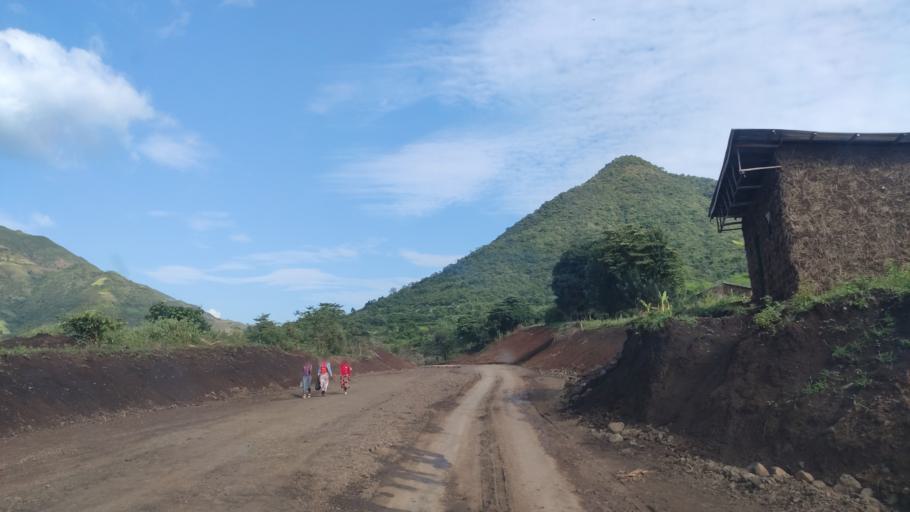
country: ET
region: Southern Nations, Nationalities, and People's Region
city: Arba Minch'
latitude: 6.4255
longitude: 37.3355
